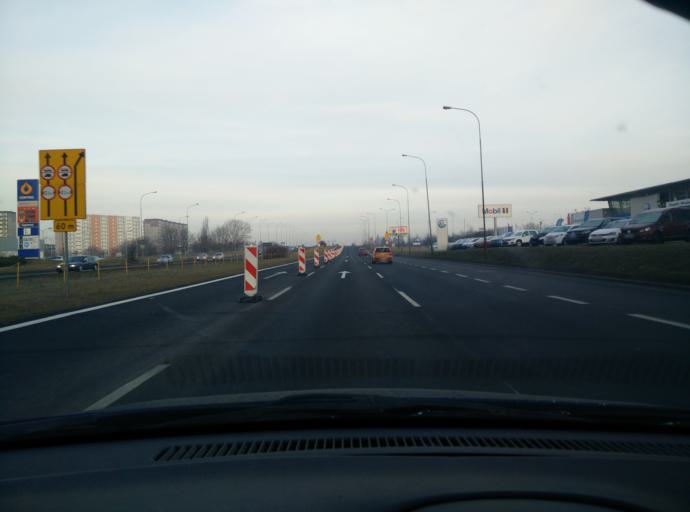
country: PL
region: Greater Poland Voivodeship
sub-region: Poznan
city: Poznan
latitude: 52.3823
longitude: 16.9750
